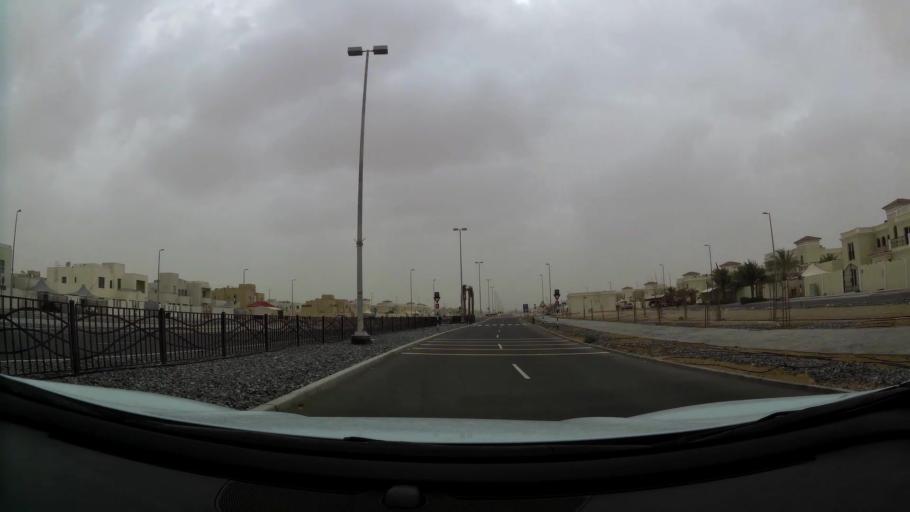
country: AE
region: Abu Dhabi
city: Abu Dhabi
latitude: 24.4564
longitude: 54.7111
